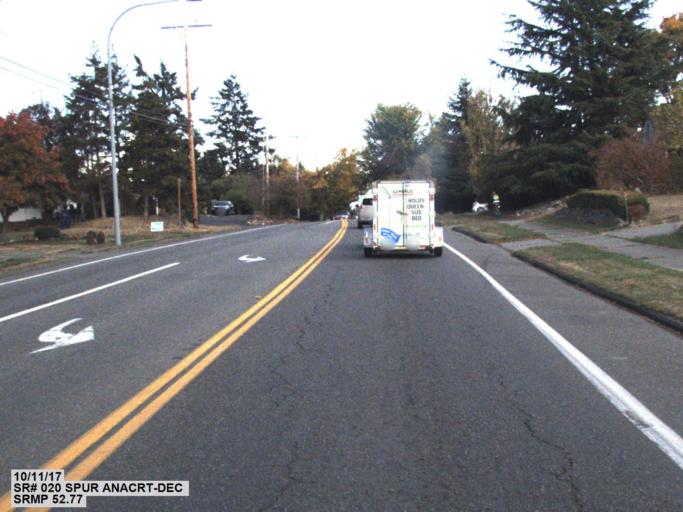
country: US
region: Washington
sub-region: Jefferson County
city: Port Hadlock-Irondale
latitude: 48.0304
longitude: -122.8265
